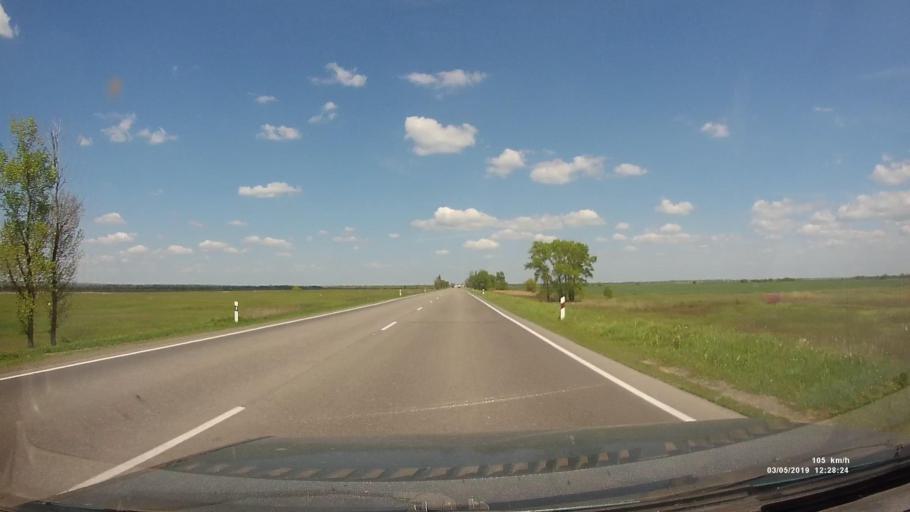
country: RU
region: Rostov
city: Semikarakorsk
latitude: 47.4730
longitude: 40.7280
